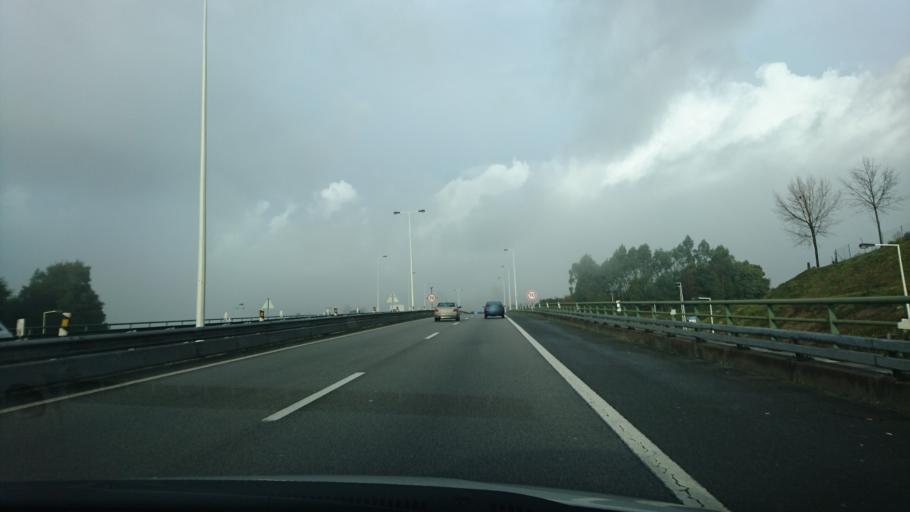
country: PT
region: Porto
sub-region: Gondomar
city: Valbom
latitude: 41.1571
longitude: -8.5601
